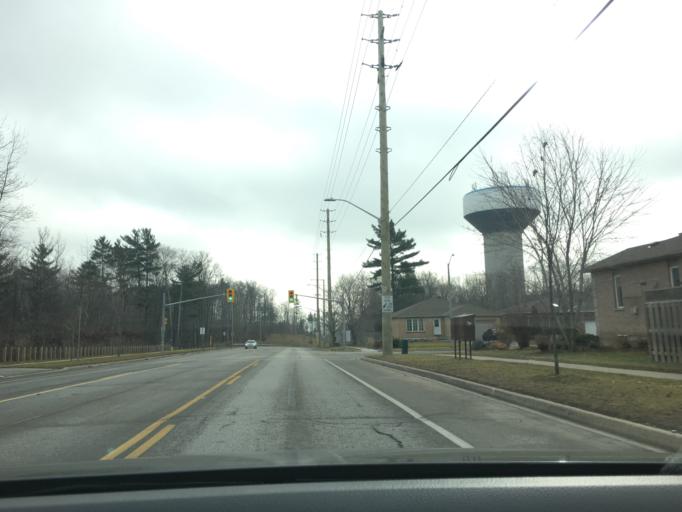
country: CA
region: Ontario
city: Barrie
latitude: 44.3929
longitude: -79.7347
